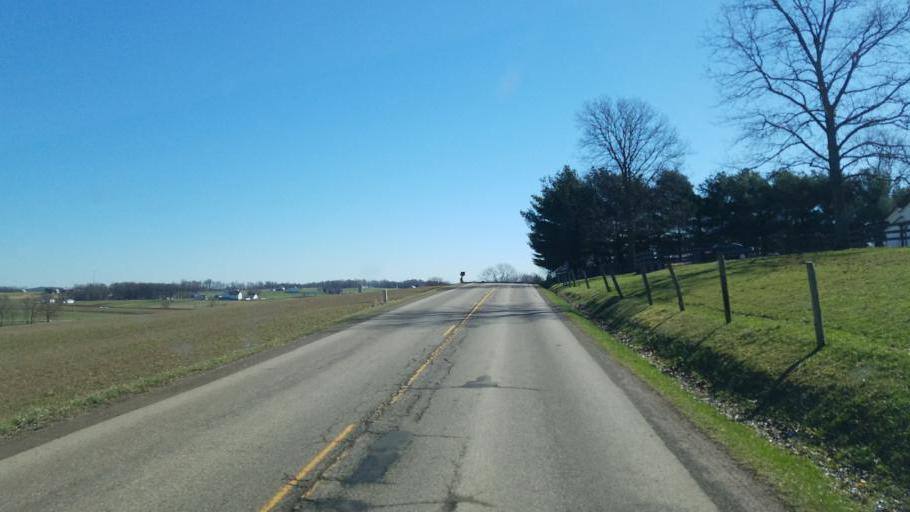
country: US
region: Ohio
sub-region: Wayne County
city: Apple Creek
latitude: 40.6973
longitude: -81.7689
